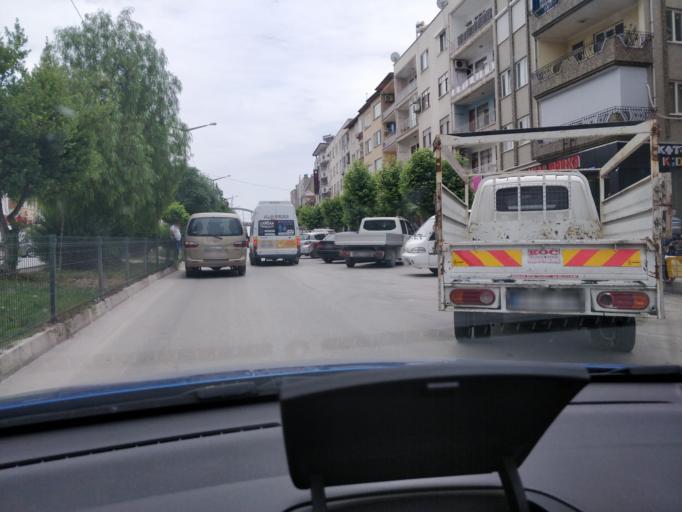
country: TR
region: Mersin
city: Mut
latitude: 36.6440
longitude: 33.4388
